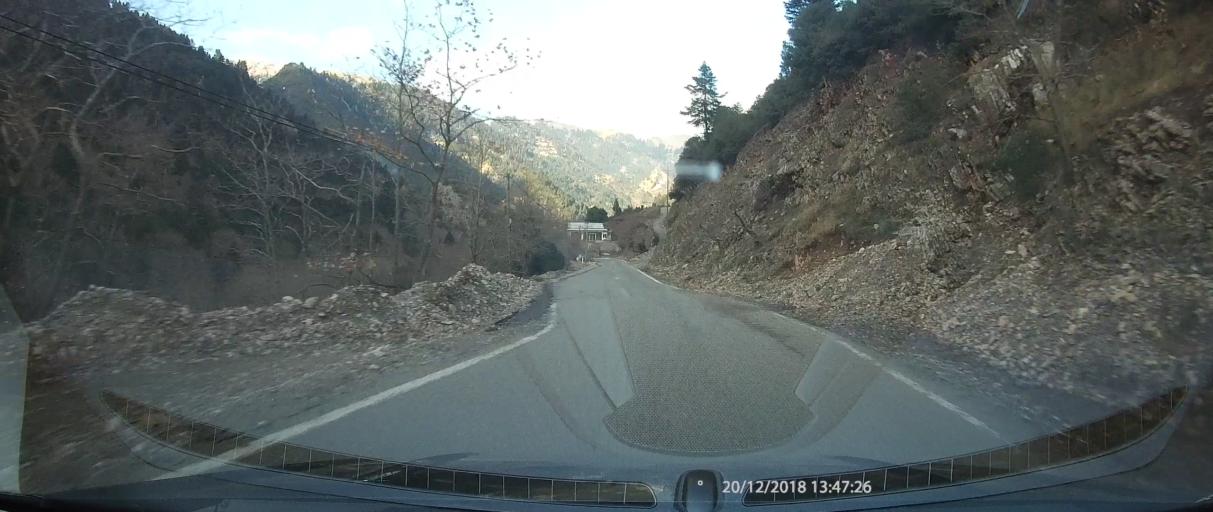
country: GR
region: West Greece
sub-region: Nomos Aitolias kai Akarnanias
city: Thermo
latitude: 38.6811
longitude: 21.6141
